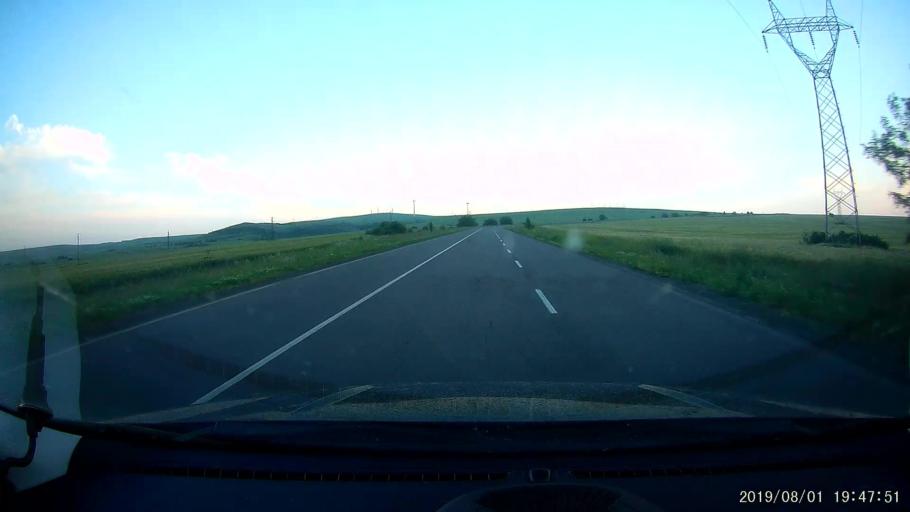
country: BG
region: Burgas
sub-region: Obshtina Karnobat
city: Karnobat
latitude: 42.6451
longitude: 26.9573
